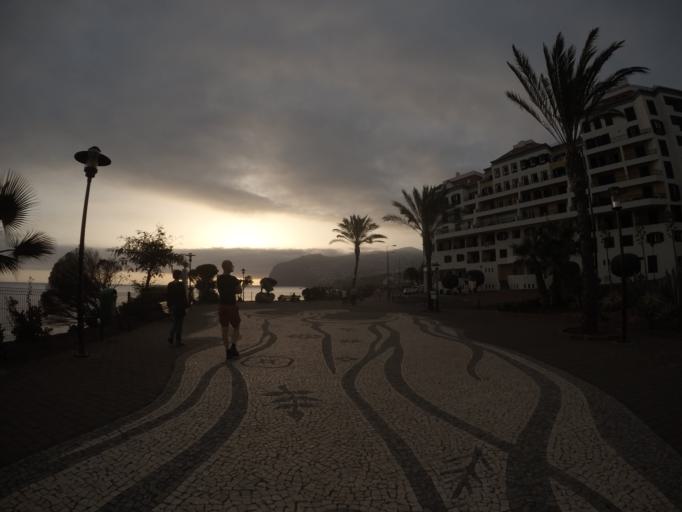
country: PT
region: Madeira
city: Camara de Lobos
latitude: 32.6340
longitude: -16.9464
